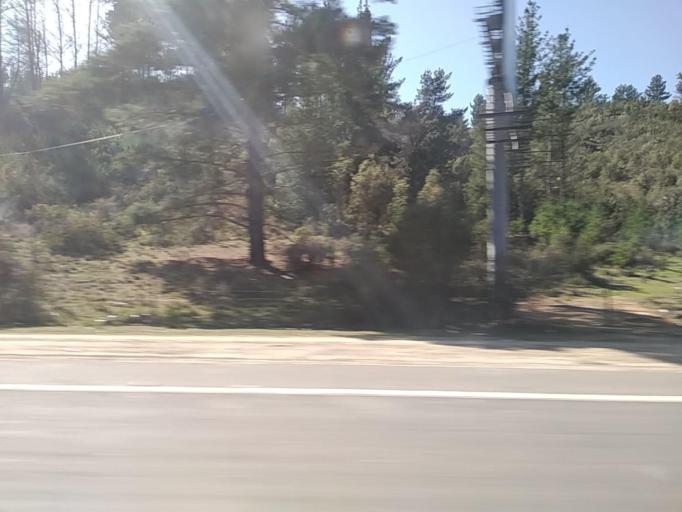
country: CL
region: Valparaiso
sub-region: Provincia de Marga Marga
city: Quilpue
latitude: -33.2306
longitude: -71.4651
